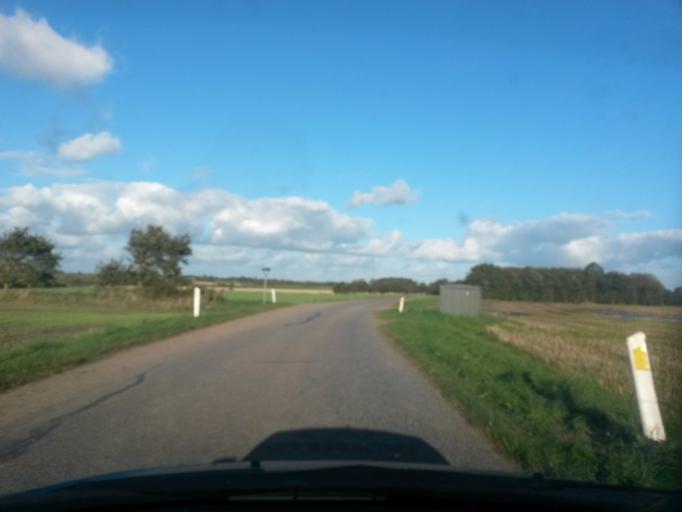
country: DK
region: Central Jutland
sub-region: Silkeborg Kommune
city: Kjellerup
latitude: 56.3345
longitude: 9.3932
